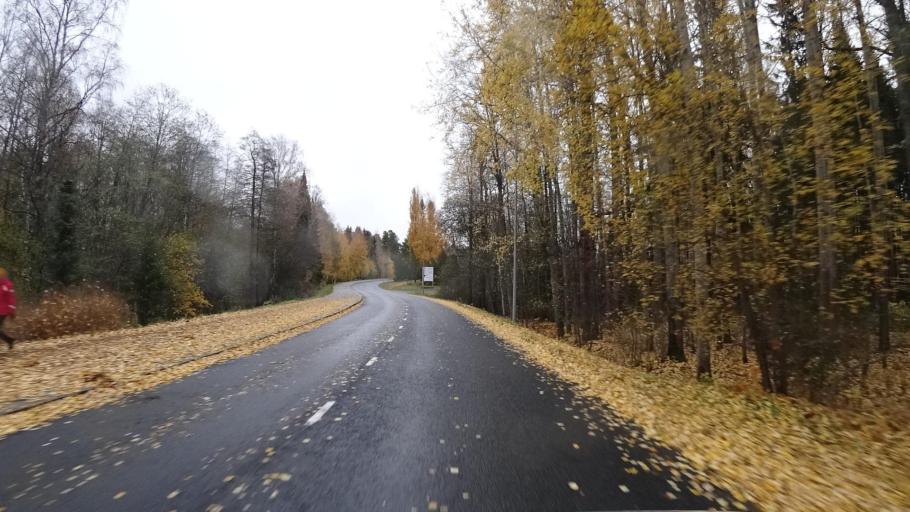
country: FI
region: Northern Savo
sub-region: Kuopio
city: Kuopio
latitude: 62.9313
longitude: 27.6800
